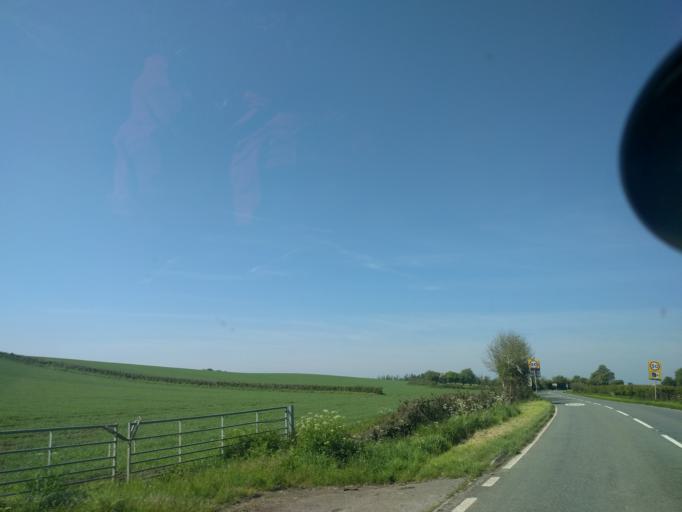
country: GB
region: England
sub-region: Somerset
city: Ilchester
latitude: 51.0266
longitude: -2.6843
